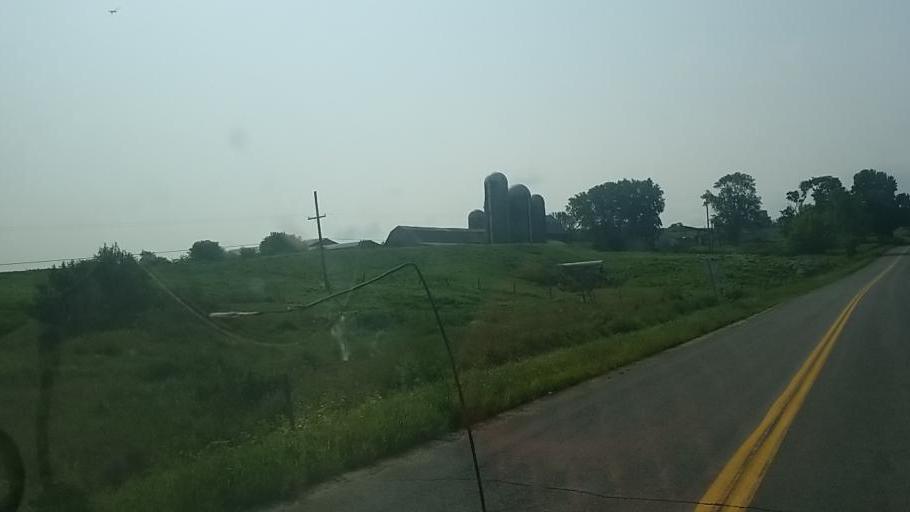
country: US
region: New York
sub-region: Montgomery County
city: Fonda
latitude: 42.9864
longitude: -74.4475
